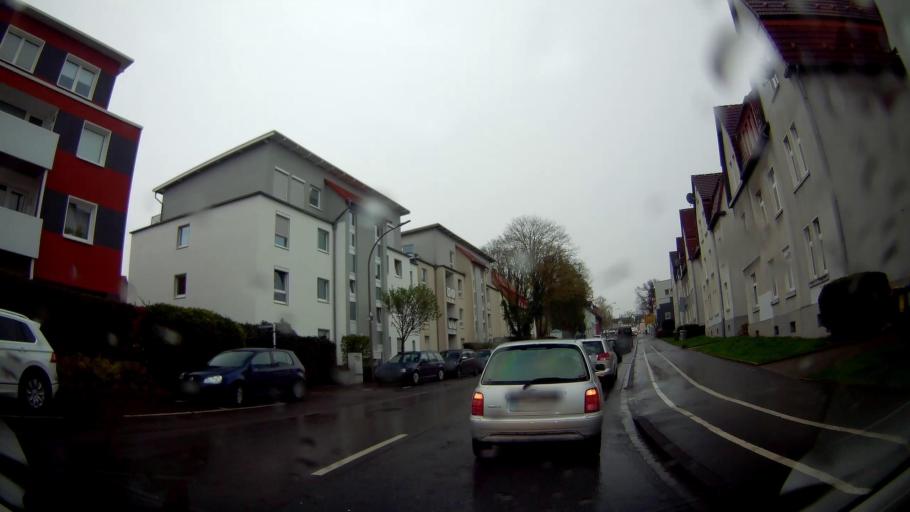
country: DE
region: North Rhine-Westphalia
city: Castrop-Rauxel
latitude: 51.5246
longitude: 7.3699
